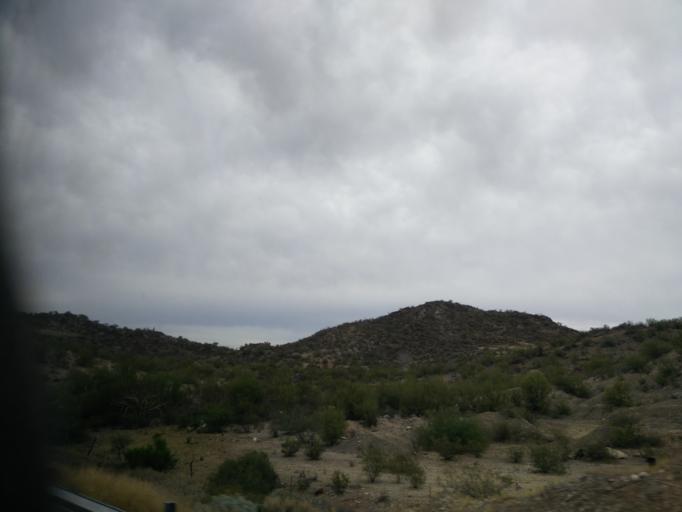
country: MX
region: Sonora
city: Hermosillo
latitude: 28.9787
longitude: -110.9645
